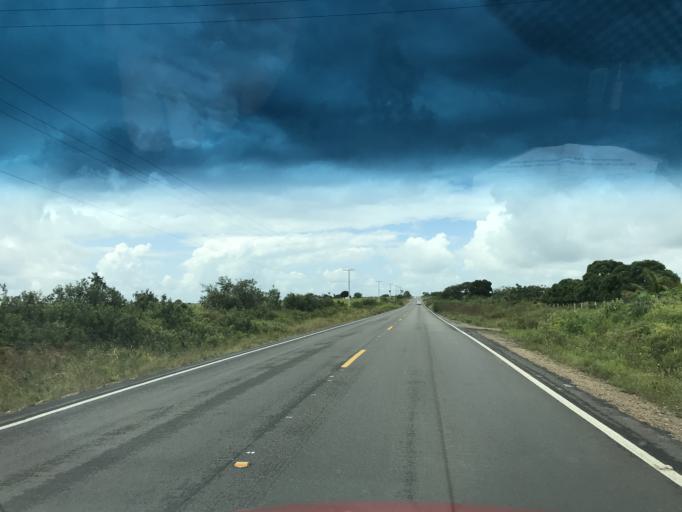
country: BR
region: Bahia
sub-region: Conceicao Do Almeida
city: Conceicao do Almeida
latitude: -12.6689
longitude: -39.2777
